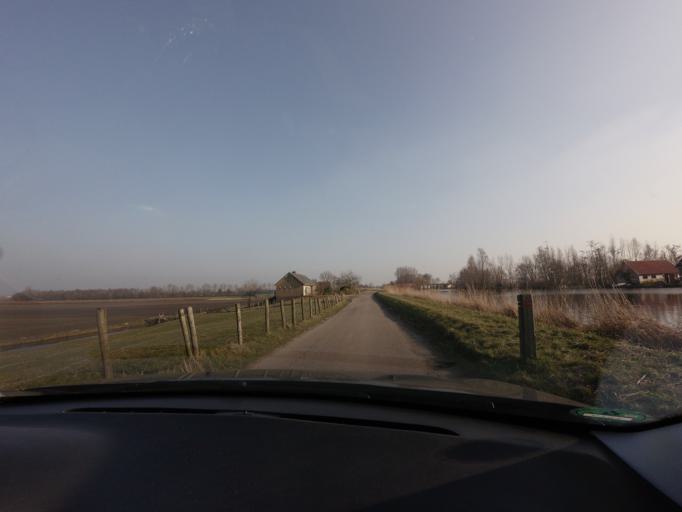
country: NL
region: South Holland
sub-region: Gemeente Kaag en Braassem
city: Leimuiden
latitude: 52.2181
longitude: 4.7031
